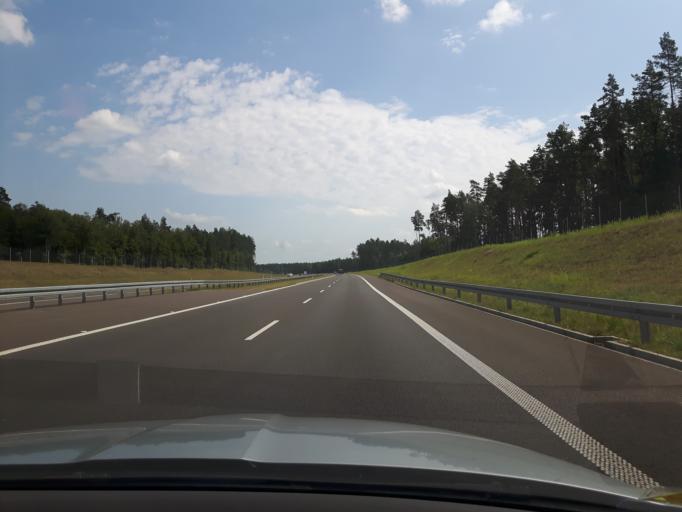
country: PL
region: Warmian-Masurian Voivodeship
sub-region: Powiat ostrodzki
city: Gierzwald
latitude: 53.5857
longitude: 20.1576
